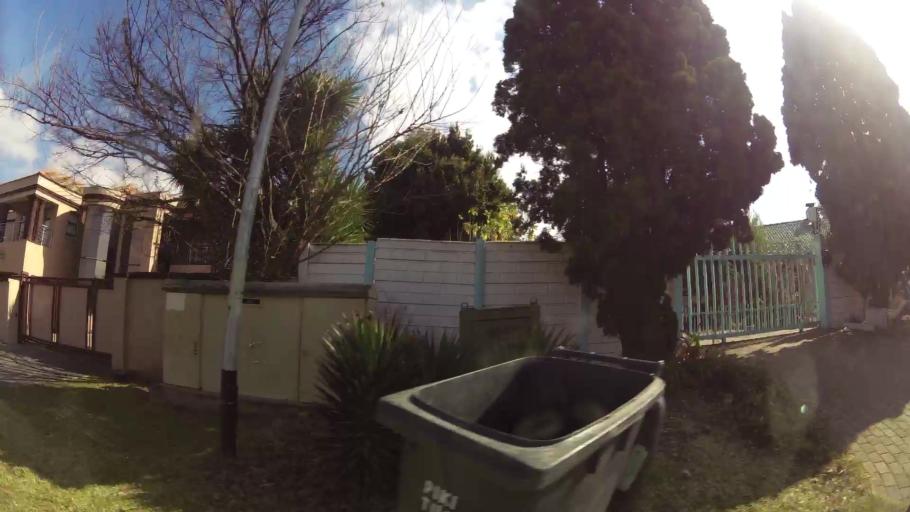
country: ZA
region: Gauteng
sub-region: City of Johannesburg Metropolitan Municipality
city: Midrand
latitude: -25.9986
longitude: 28.1074
